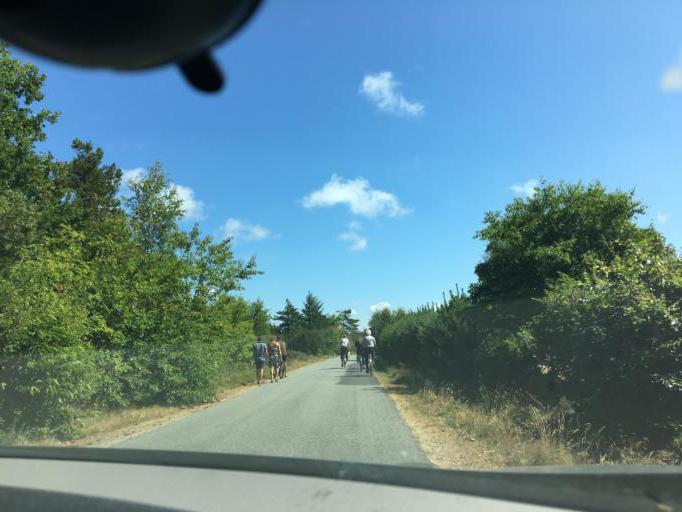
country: DK
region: South Denmark
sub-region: Varde Kommune
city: Oksbol
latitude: 55.7359
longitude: 8.2092
